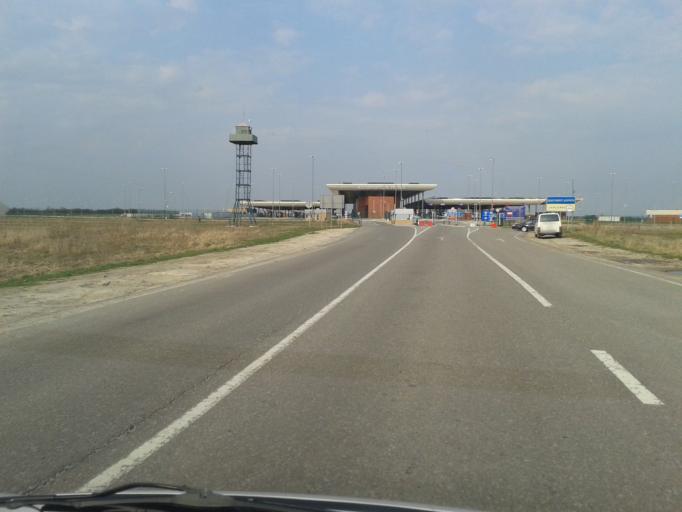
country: PL
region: Lublin Voivodeship
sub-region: Powiat hrubieszowski
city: Dolhobyczow
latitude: 50.5779
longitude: 24.0925
